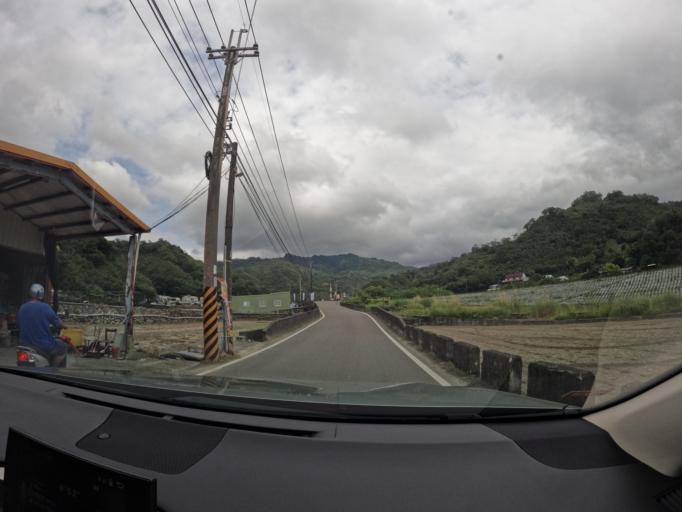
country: TW
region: Taiwan
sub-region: Miaoli
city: Miaoli
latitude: 24.4285
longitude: 120.8776
